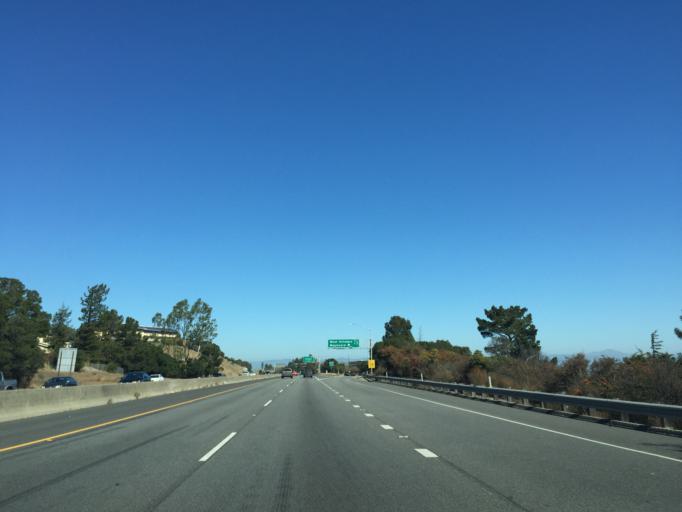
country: US
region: California
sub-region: San Mateo County
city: Highlands-Baywood Park
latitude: 37.5290
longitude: -122.3309
